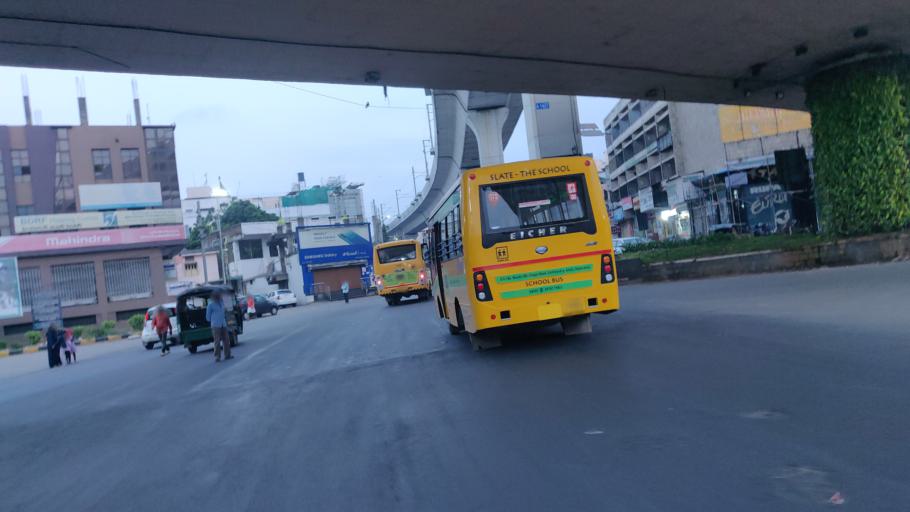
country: IN
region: Telangana
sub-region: Rangareddi
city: Gaddi Annaram
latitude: 17.3754
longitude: 78.4983
